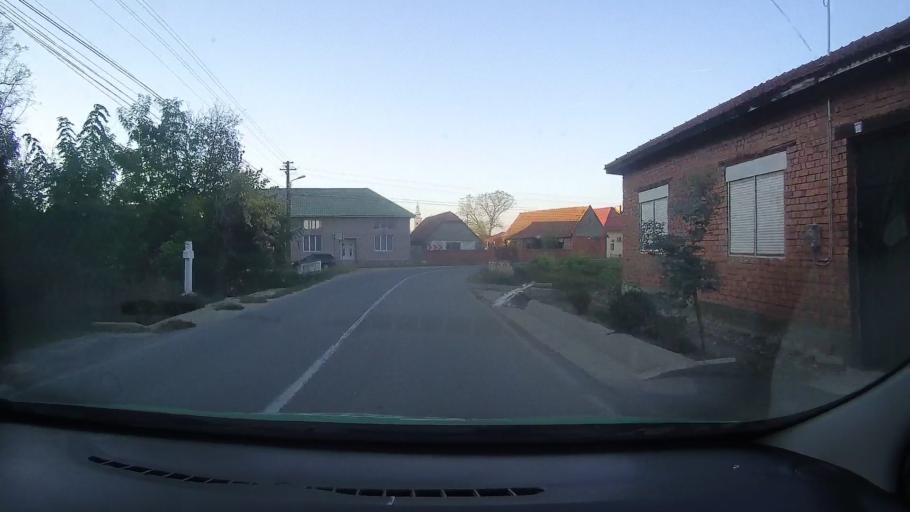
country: RO
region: Timis
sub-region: Comuna Traian Vuia
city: Traian Vuia
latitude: 45.7647
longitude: 22.0953
